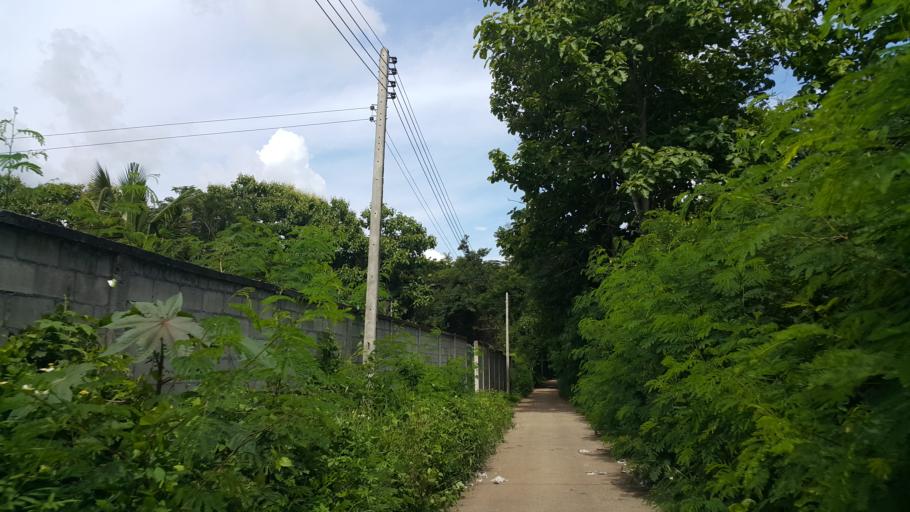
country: TH
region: Chiang Mai
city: Mae On
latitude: 18.7442
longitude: 99.1952
